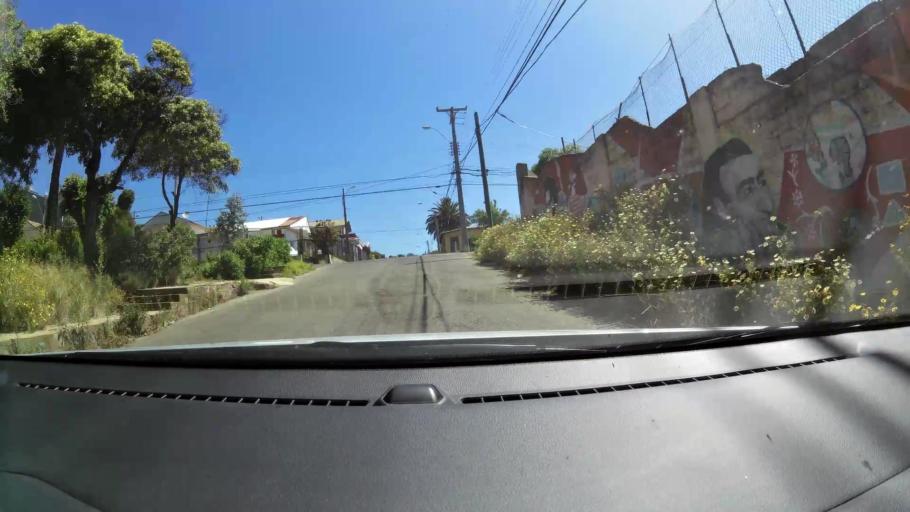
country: CL
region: Valparaiso
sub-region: Provincia de Valparaiso
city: Valparaiso
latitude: -33.0290
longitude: -71.6387
